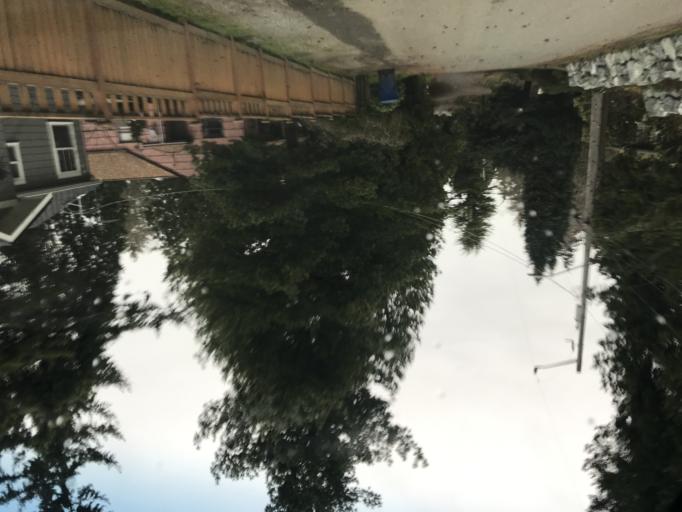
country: US
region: Washington
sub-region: King County
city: Lake Forest Park
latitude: 47.7058
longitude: -122.3033
